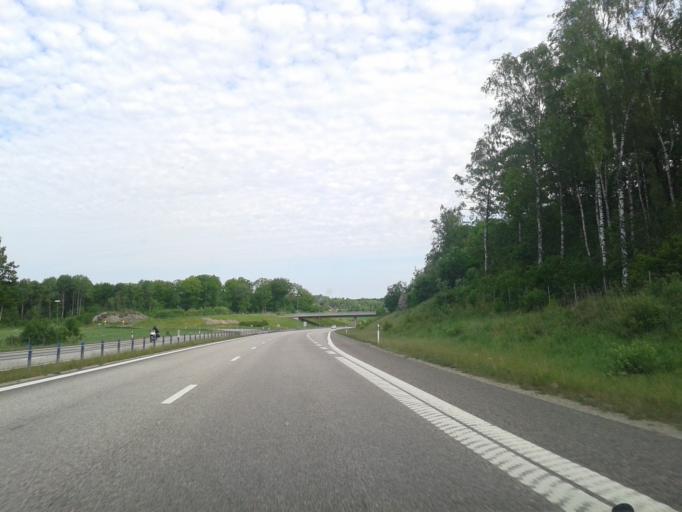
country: SE
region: Vaestra Goetaland
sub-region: Munkedals Kommun
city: Munkedal
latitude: 58.4575
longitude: 11.6617
